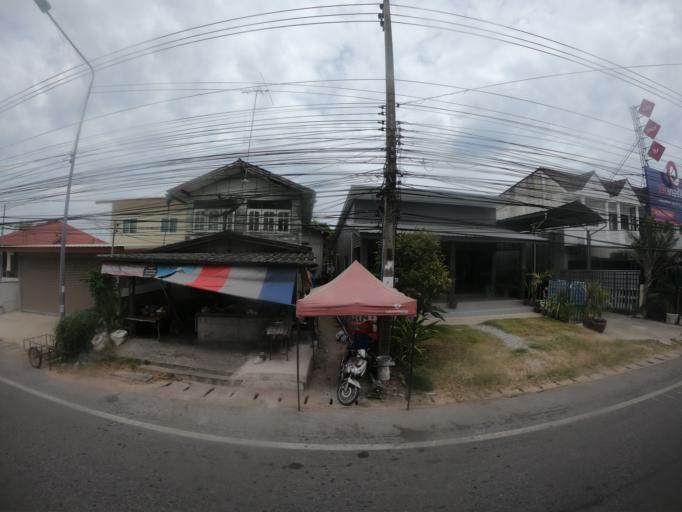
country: TH
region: Maha Sarakham
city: Maha Sarakham
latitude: 16.1722
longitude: 103.3193
